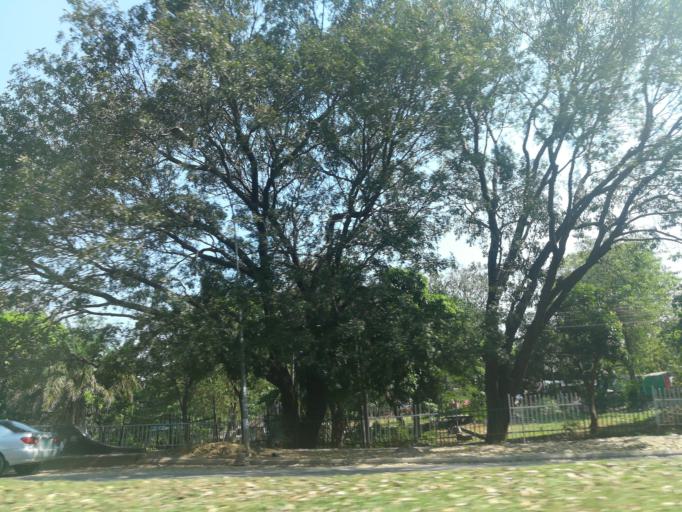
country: NG
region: Abuja Federal Capital Territory
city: Abuja
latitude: 9.0590
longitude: 7.4581
